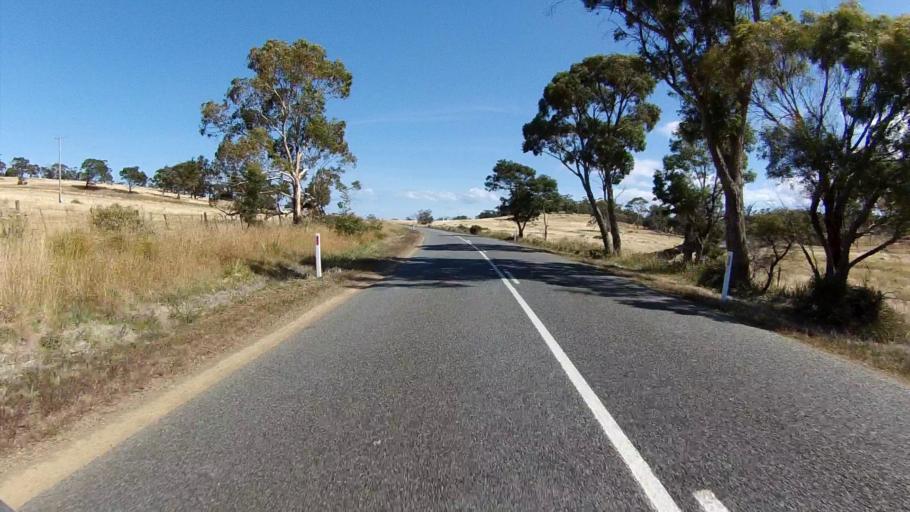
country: AU
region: Tasmania
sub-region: Sorell
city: Sorell
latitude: -42.2976
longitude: 147.9843
